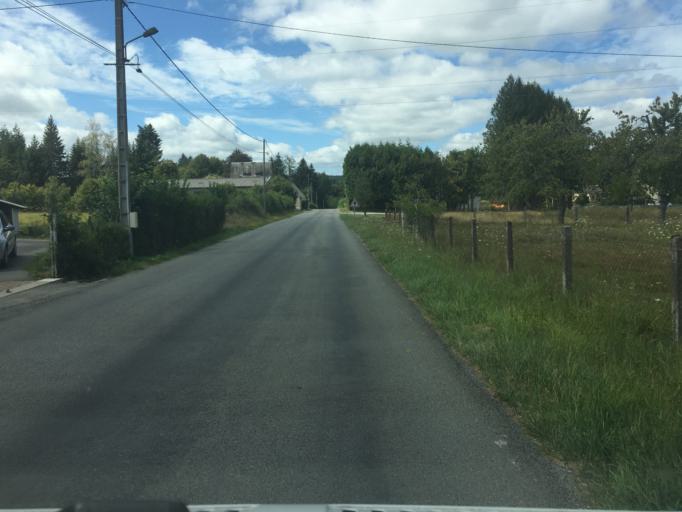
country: FR
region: Limousin
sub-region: Departement de la Correze
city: Neuvic
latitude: 45.4214
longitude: 2.3416
